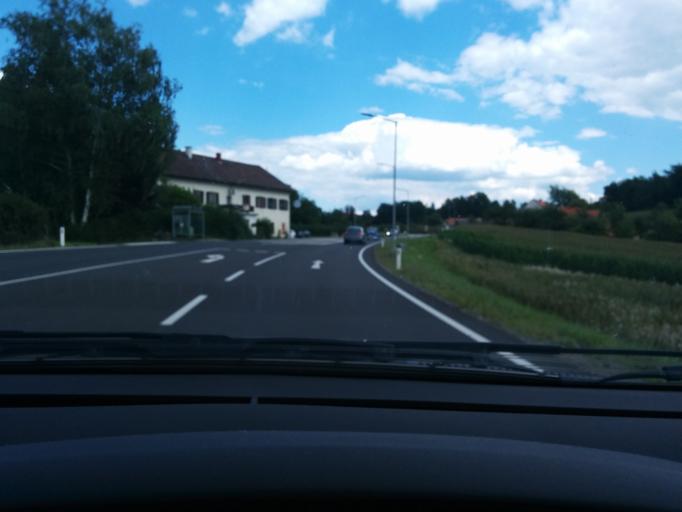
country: AT
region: Styria
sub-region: Politischer Bezirk Weiz
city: Oberrettenbach
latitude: 47.1688
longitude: 15.7785
